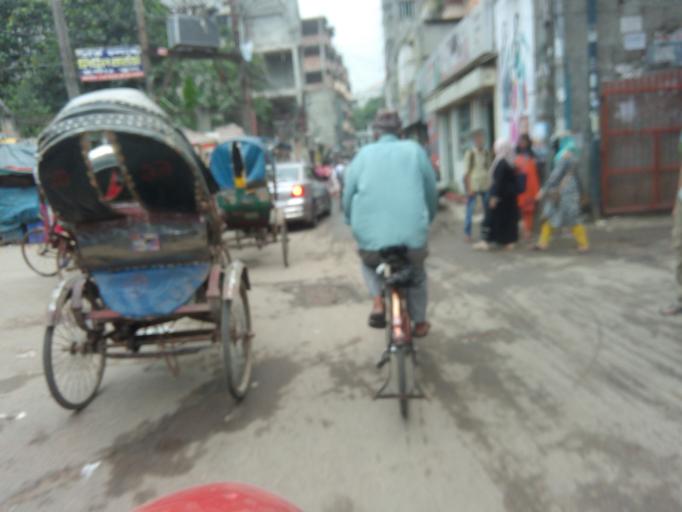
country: BD
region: Dhaka
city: Azimpur
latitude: 23.7241
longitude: 90.3840
